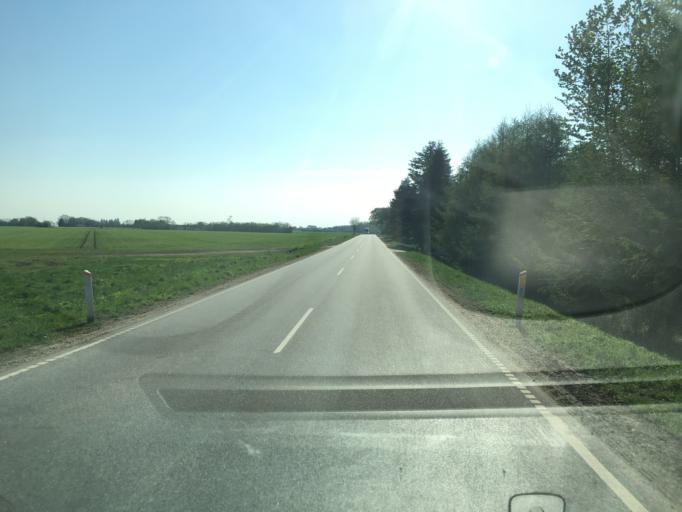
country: DK
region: South Denmark
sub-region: Tonder Kommune
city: Toftlund
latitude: 55.1973
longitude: 9.1211
